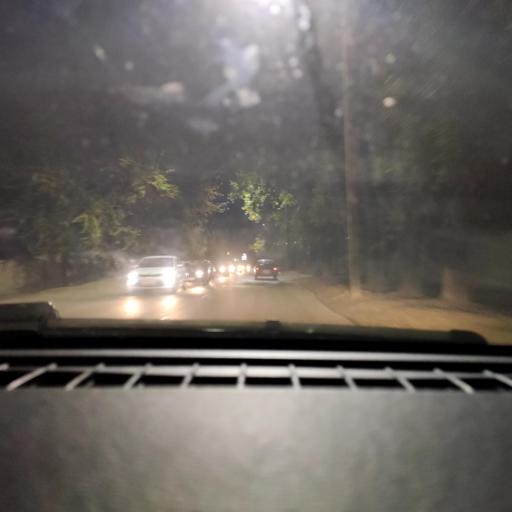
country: RU
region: Voronezj
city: Maslovka
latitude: 51.6328
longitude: 39.2626
